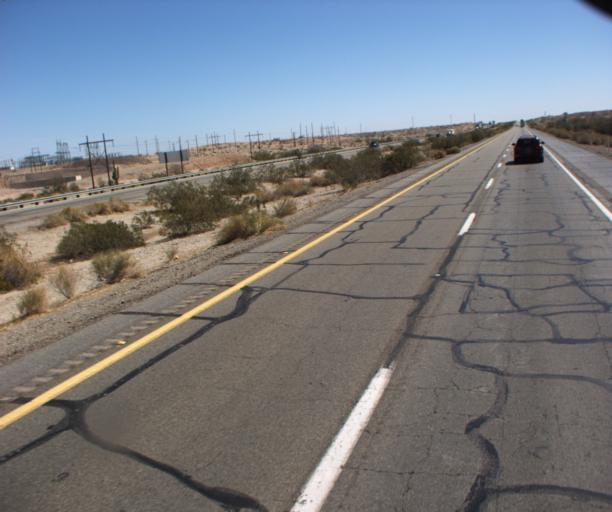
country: US
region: Arizona
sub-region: Yuma County
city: Wellton
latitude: 32.6639
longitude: -114.2715
